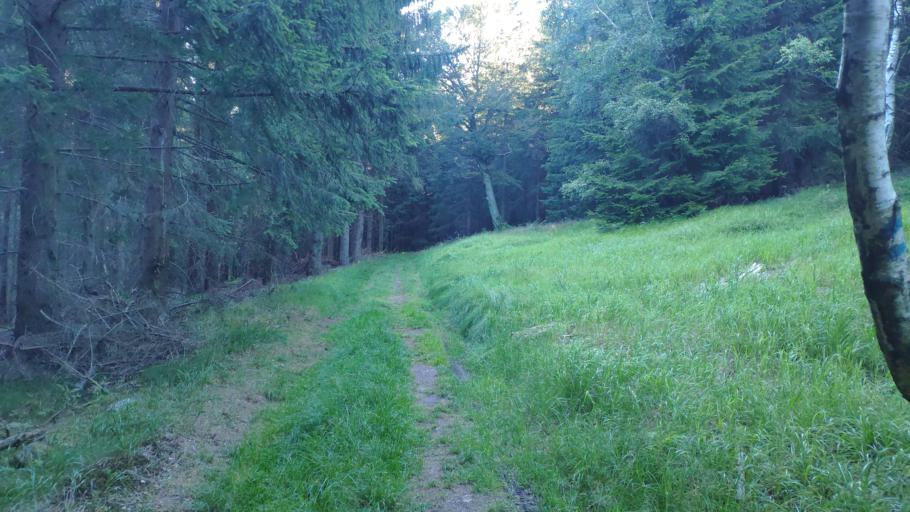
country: PL
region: Lower Silesian Voivodeship
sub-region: Powiat jeleniogorski
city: Kowary
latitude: 50.7704
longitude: 15.8668
